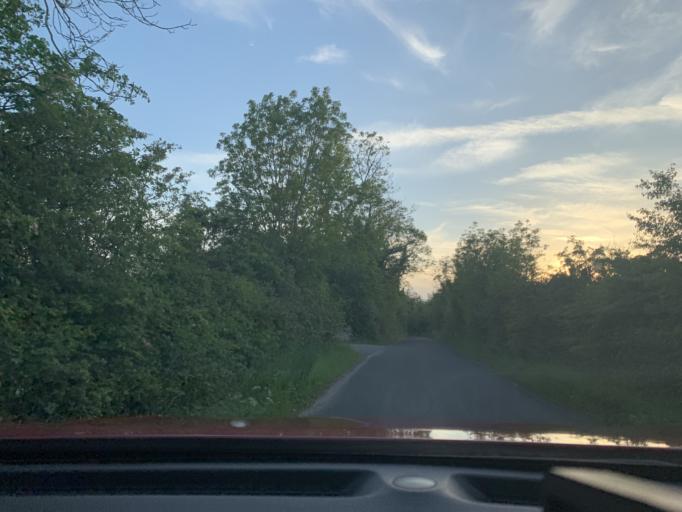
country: IE
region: Connaught
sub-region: Sligo
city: Sligo
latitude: 54.2901
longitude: -8.4538
